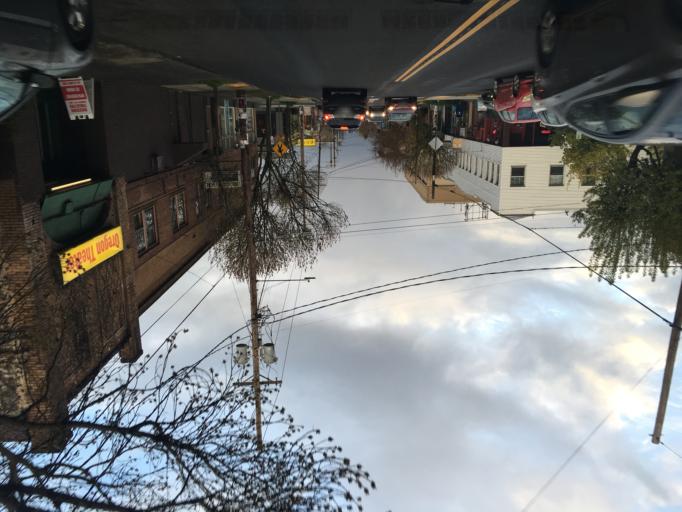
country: US
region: Oregon
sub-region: Multnomah County
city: Portland
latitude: 45.5048
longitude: -122.6281
